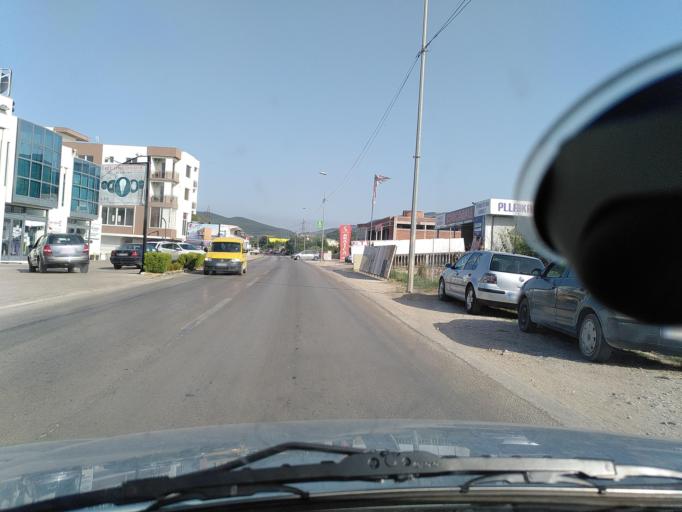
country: ME
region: Ulcinj
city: Ulcinj
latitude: 41.9351
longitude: 19.2214
